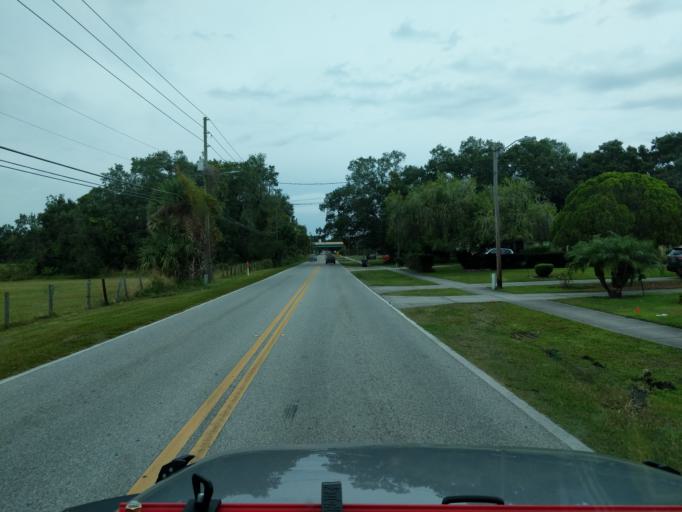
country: US
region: Florida
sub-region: Orange County
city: Oakland
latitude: 28.5410
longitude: -81.6079
